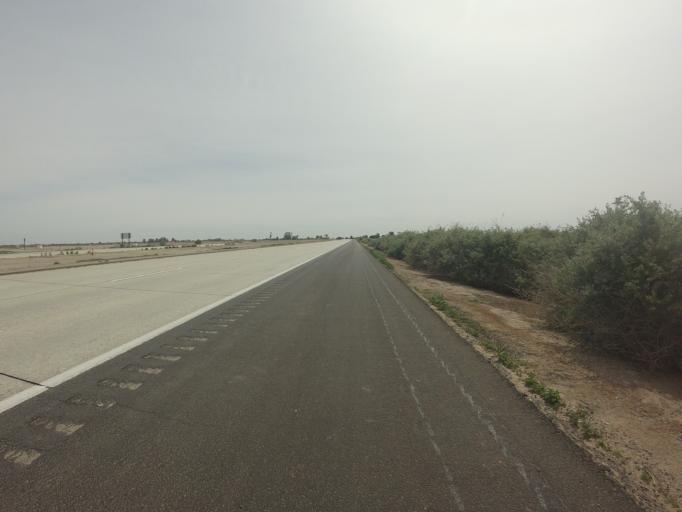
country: US
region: California
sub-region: Imperial County
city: Westmorland
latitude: 32.9979
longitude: -115.5883
